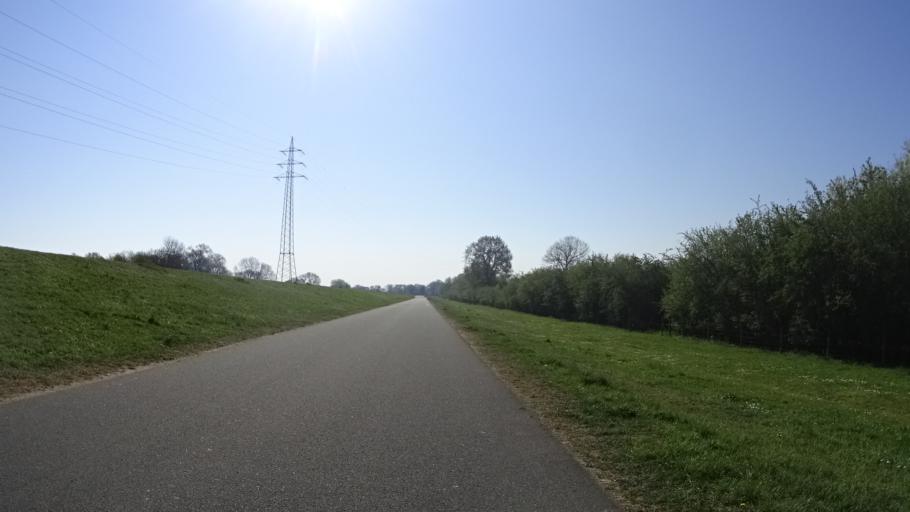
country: DE
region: North Rhine-Westphalia
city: Rheinberg
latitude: 51.5743
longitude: 6.5855
